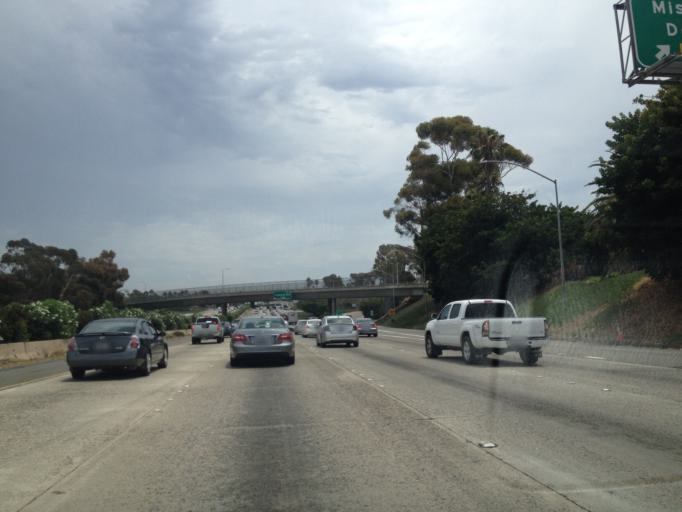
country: US
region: California
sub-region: San Diego County
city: Oceanside
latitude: 33.2018
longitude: -117.3767
